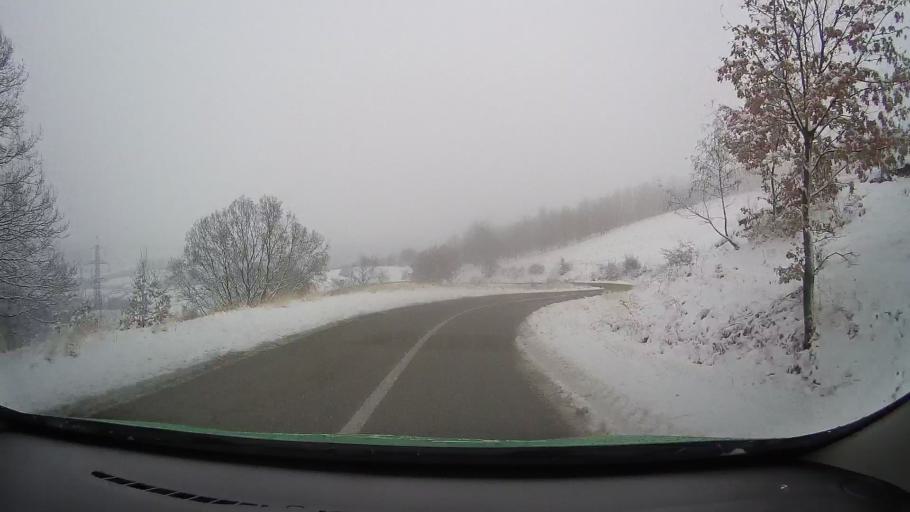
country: RO
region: Hunedoara
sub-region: Comuna Unirea
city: Unirea
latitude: 45.6606
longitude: 22.9089
